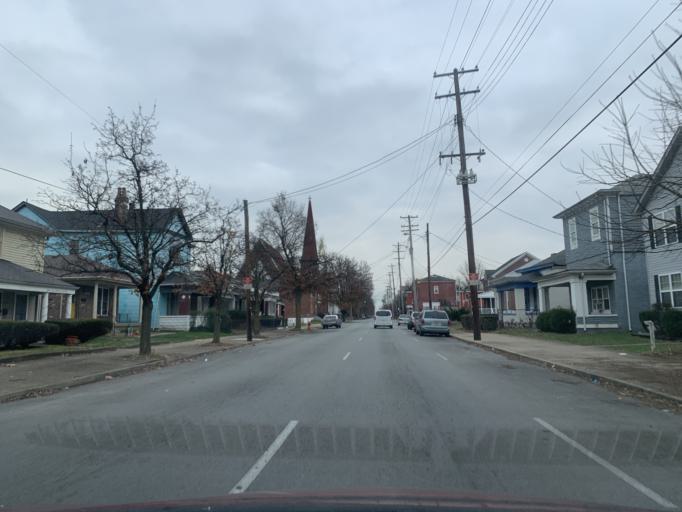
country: US
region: Kentucky
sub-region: Jefferson County
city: Louisville
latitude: 38.2517
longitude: -85.7827
